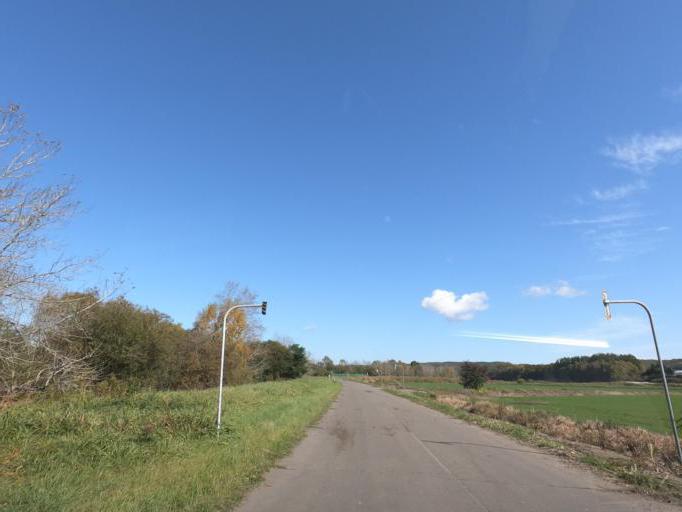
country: JP
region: Hokkaido
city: Otofuke
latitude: 43.0572
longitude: 143.2771
